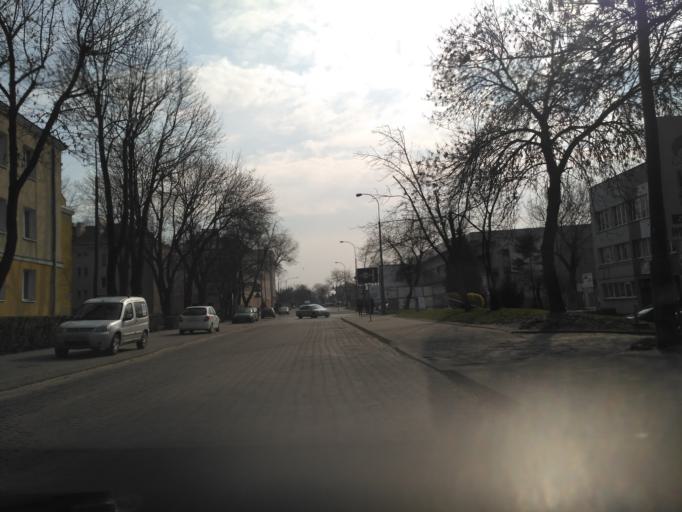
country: PL
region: Lublin Voivodeship
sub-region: Powiat lubelski
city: Lublin
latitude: 51.2349
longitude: 22.5879
